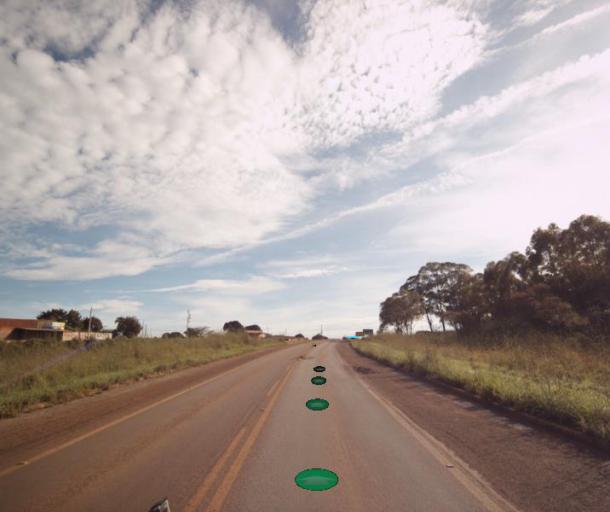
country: BR
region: Federal District
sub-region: Brasilia
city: Brasilia
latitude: -15.7411
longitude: -48.4098
